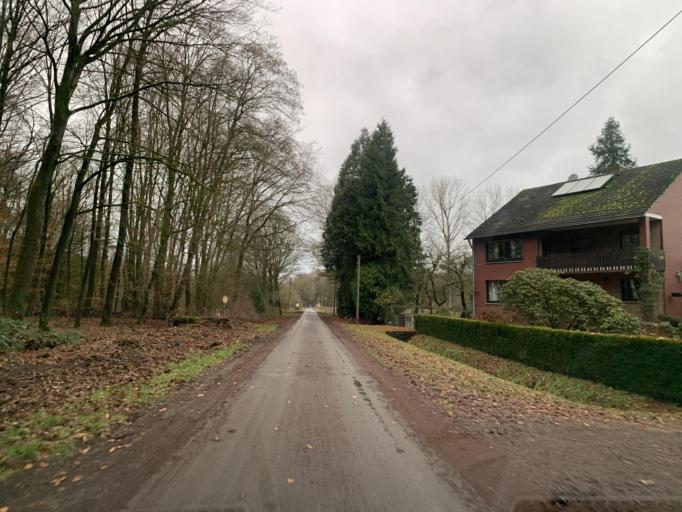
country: DE
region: North Rhine-Westphalia
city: Olfen
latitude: 51.7477
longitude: 7.3022
